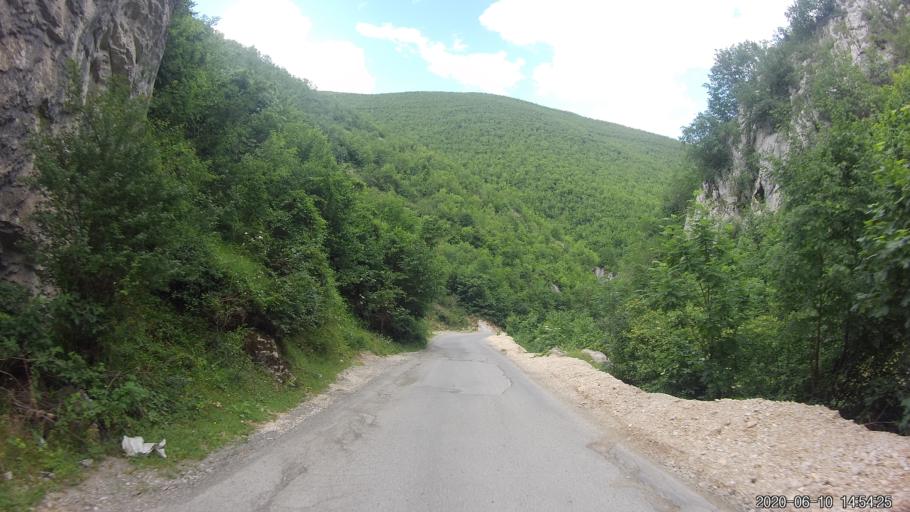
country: XK
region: Ferizaj
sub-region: Komuna e Shtimes
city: Shtime
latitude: 42.4057
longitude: 20.9929
